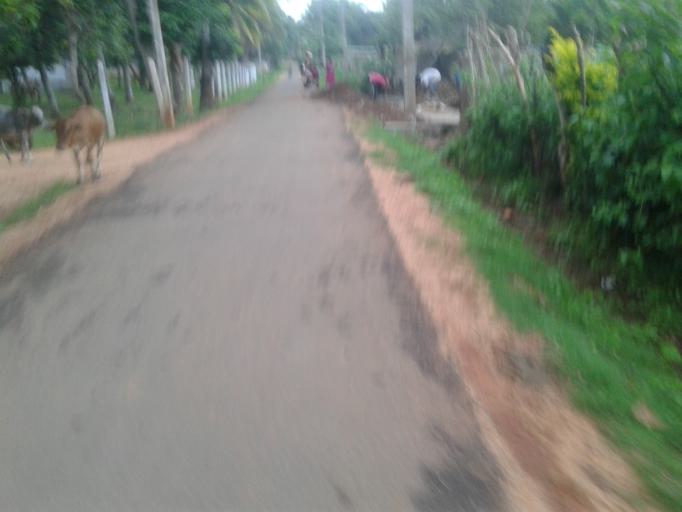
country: LK
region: Northern Province
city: Vavuniya
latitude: 8.7766
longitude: 80.4990
